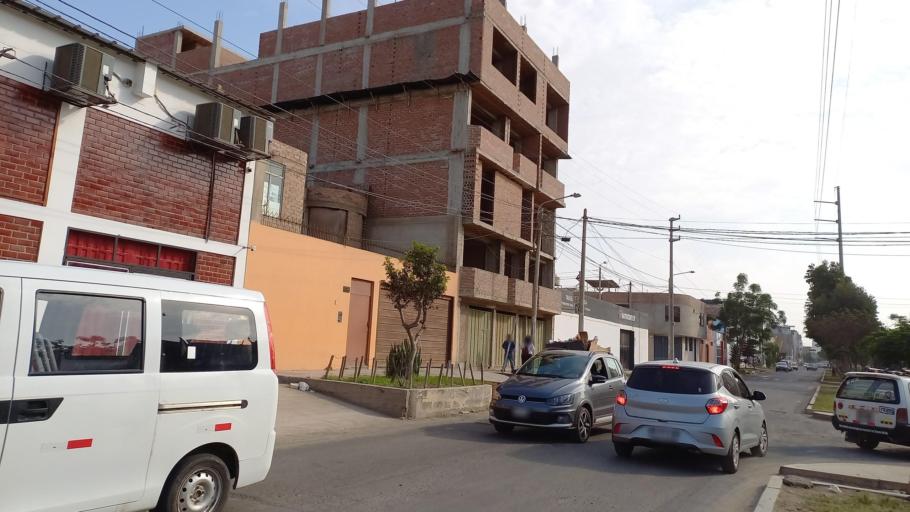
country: PE
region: La Libertad
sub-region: Provincia de Trujillo
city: Trujillo
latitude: -8.1183
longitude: -79.0458
